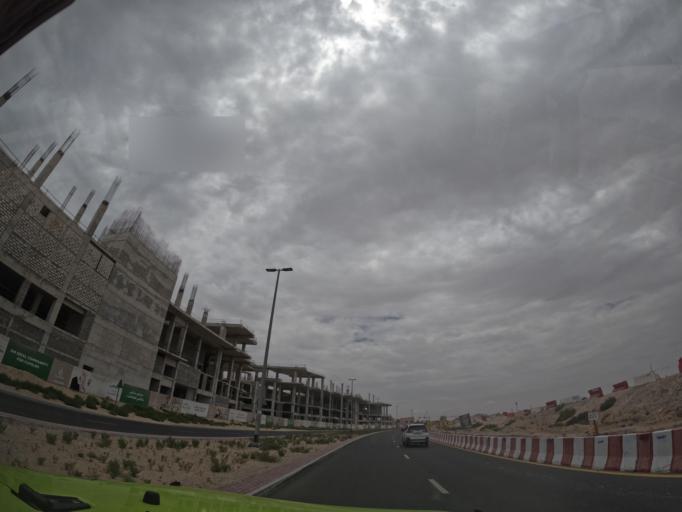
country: AE
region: Ash Shariqah
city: Sharjah
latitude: 25.1596
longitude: 55.3683
